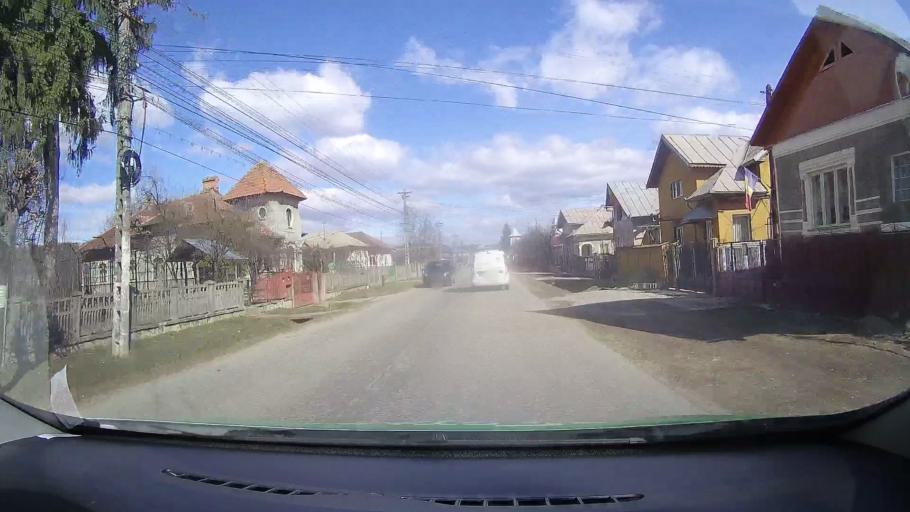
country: RO
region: Dambovita
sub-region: Comuna Branesti
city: Branesti
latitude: 45.0323
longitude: 25.4119
